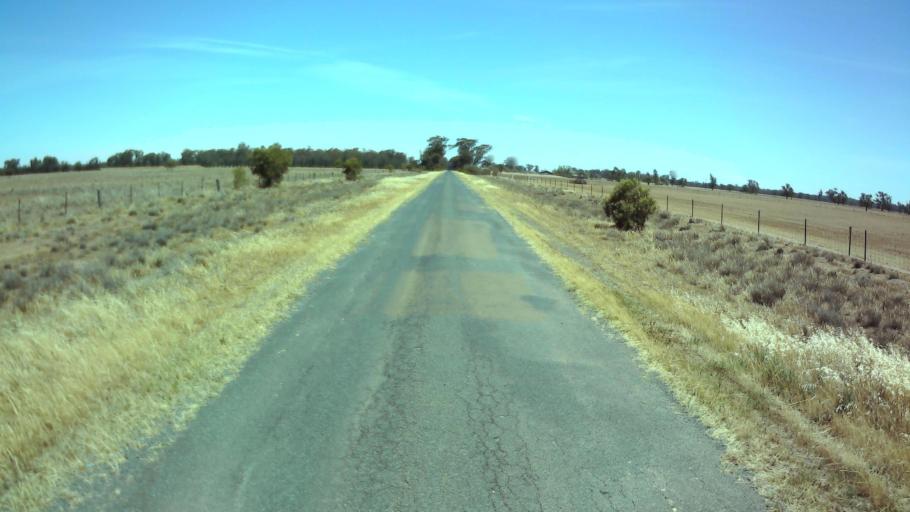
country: AU
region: New South Wales
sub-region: Weddin
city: Grenfell
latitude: -33.8969
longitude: 147.6871
